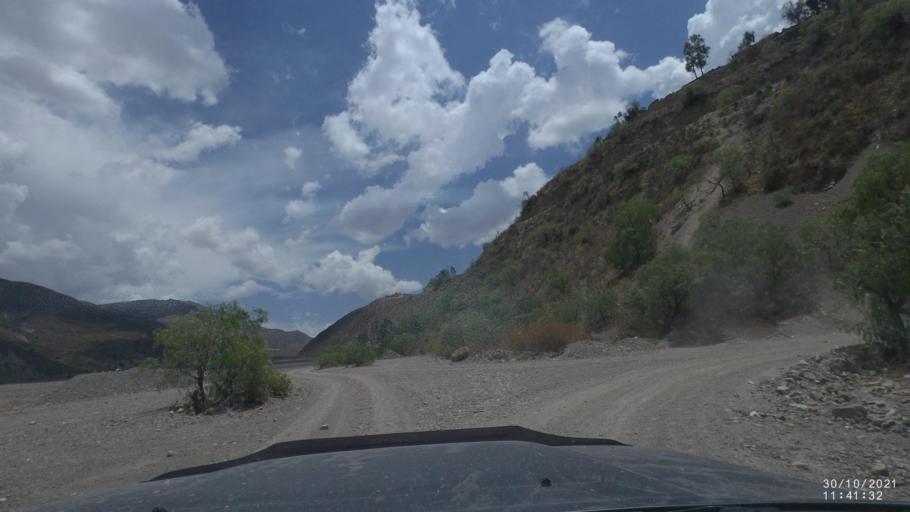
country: BO
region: Cochabamba
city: Colchani
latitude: -17.5166
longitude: -66.6232
